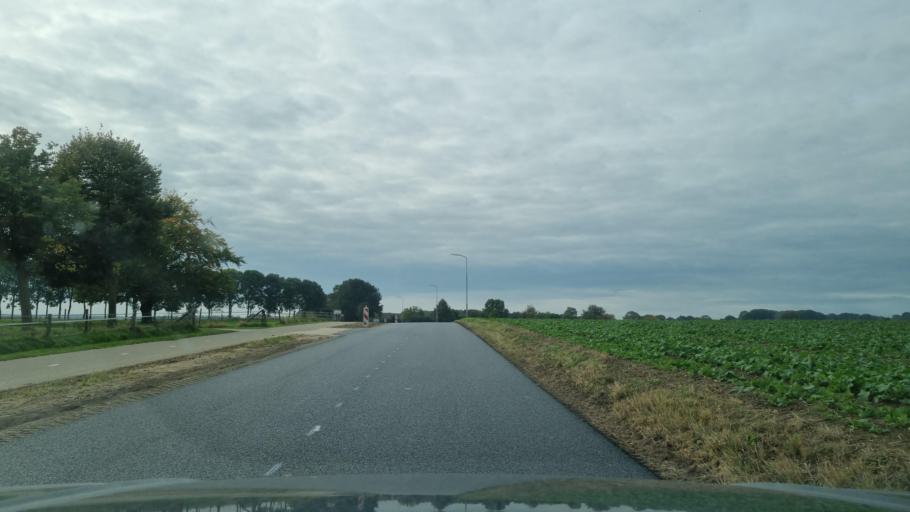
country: NL
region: Gelderland
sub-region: Gemeente Groesbeek
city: De Horst
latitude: 51.7986
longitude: 5.9545
